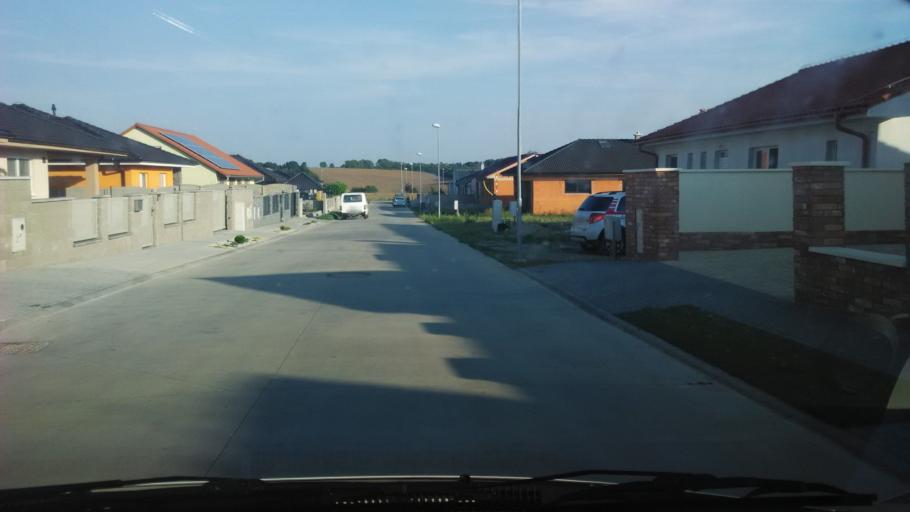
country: SK
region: Nitriansky
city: Levice
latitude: 48.2151
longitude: 18.6290
